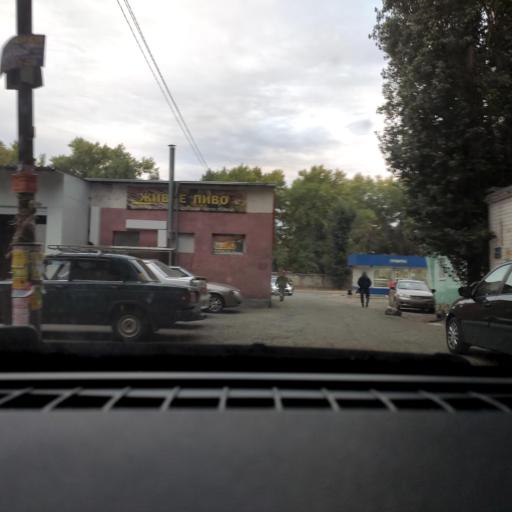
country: RU
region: Voronezj
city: Voronezh
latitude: 51.6384
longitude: 39.2668
